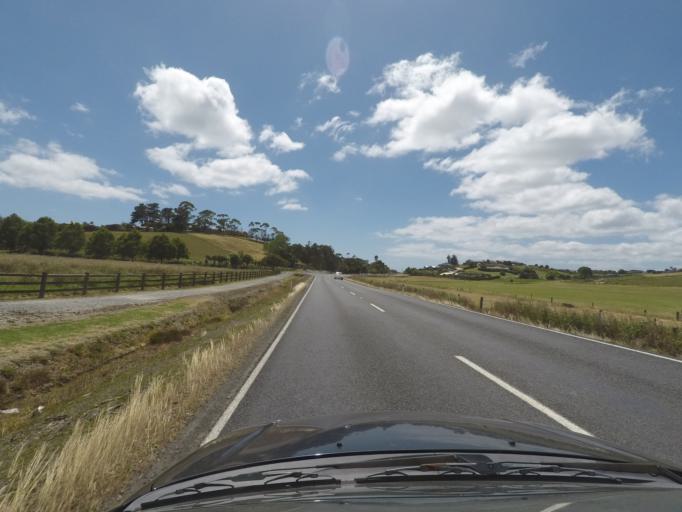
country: NZ
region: Northland
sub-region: Whangarei
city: Ruakaka
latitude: -35.9937
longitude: 174.4640
